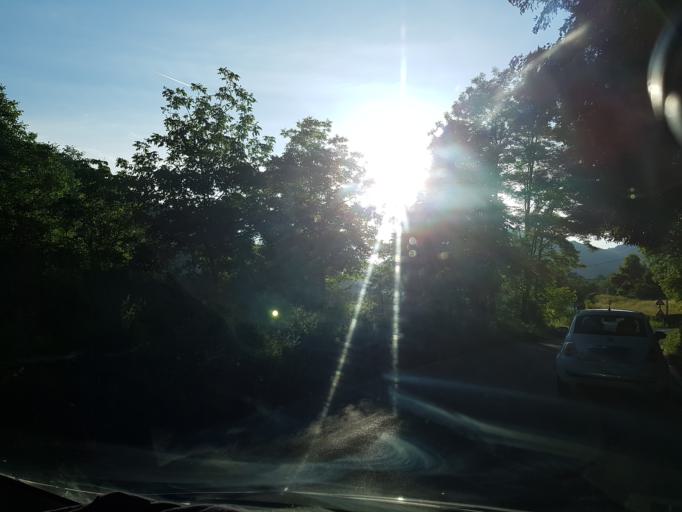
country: IT
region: Tuscany
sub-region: Provincia di Massa-Carrara
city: Casola in Lunigiana
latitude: 44.1952
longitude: 10.1902
